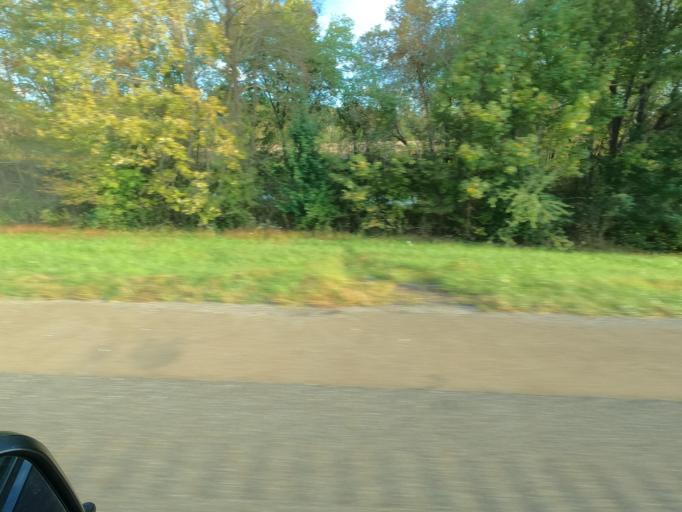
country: US
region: Tennessee
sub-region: Humphreys County
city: New Johnsonville
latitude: 35.8476
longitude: -88.0724
